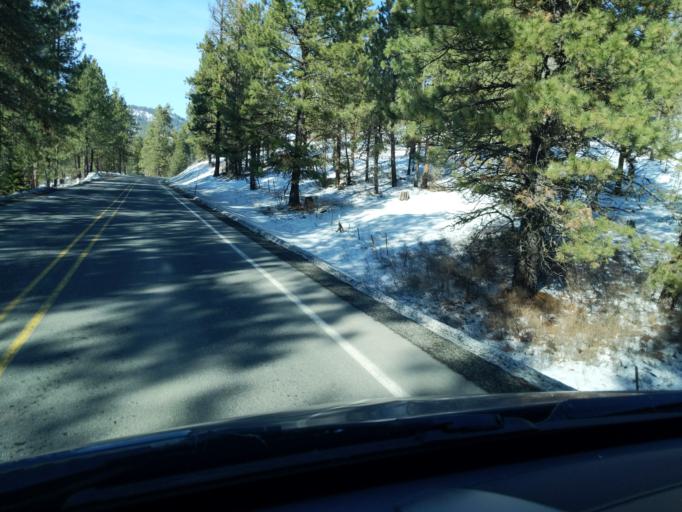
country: US
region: Oregon
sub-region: Grant County
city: John Day
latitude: 44.9160
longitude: -119.0088
